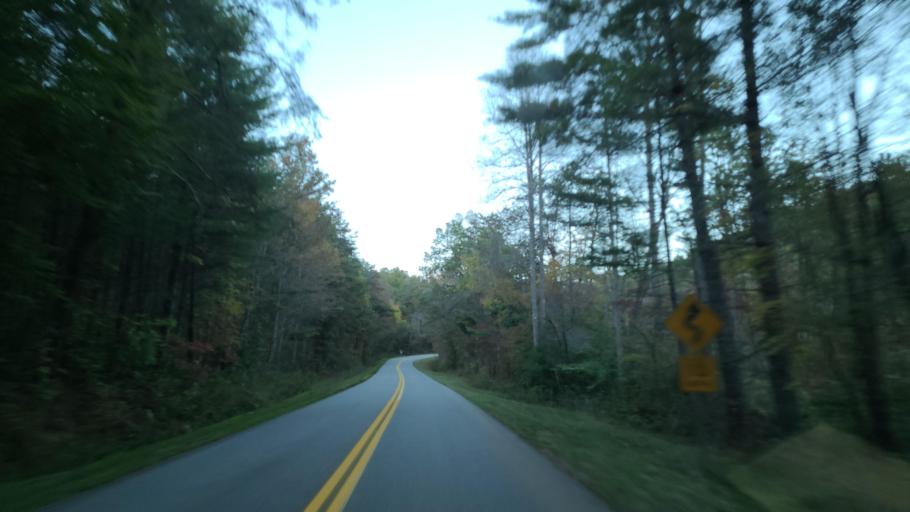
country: US
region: Georgia
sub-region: Union County
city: Blairsville
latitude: 34.8801
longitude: -83.8783
